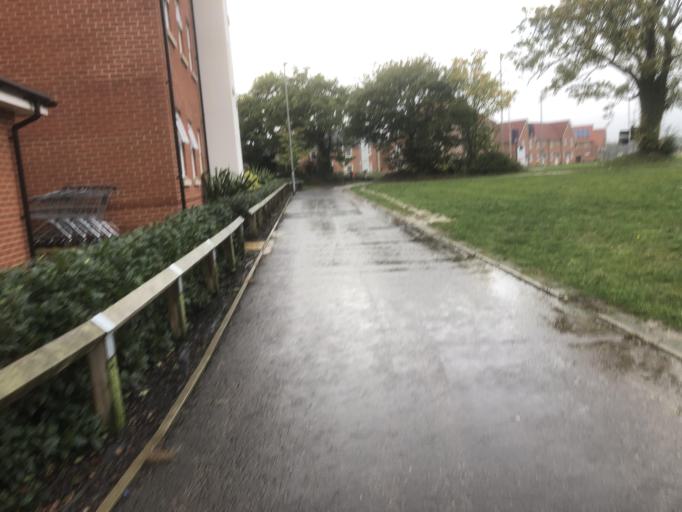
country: GB
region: England
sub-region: Norfolk
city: Spixworth
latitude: 52.6575
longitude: 1.3483
